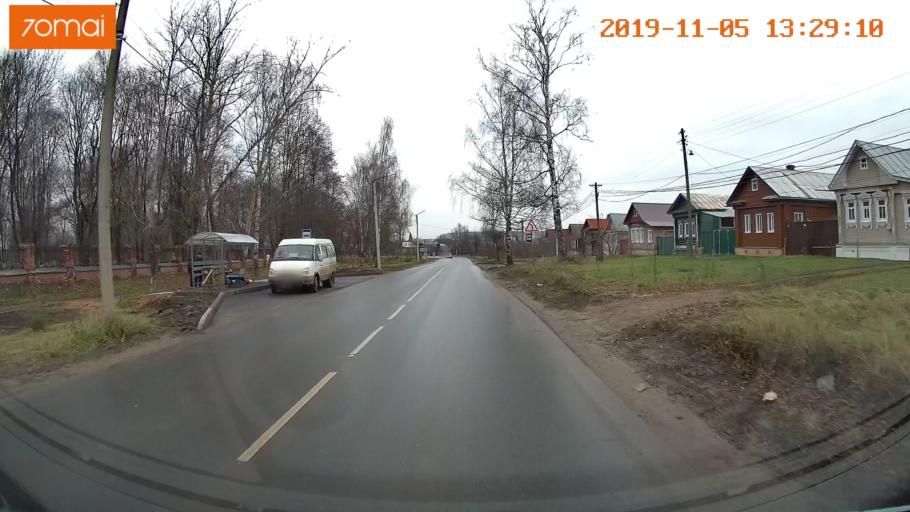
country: RU
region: Ivanovo
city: Shuya
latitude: 56.8589
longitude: 41.3955
